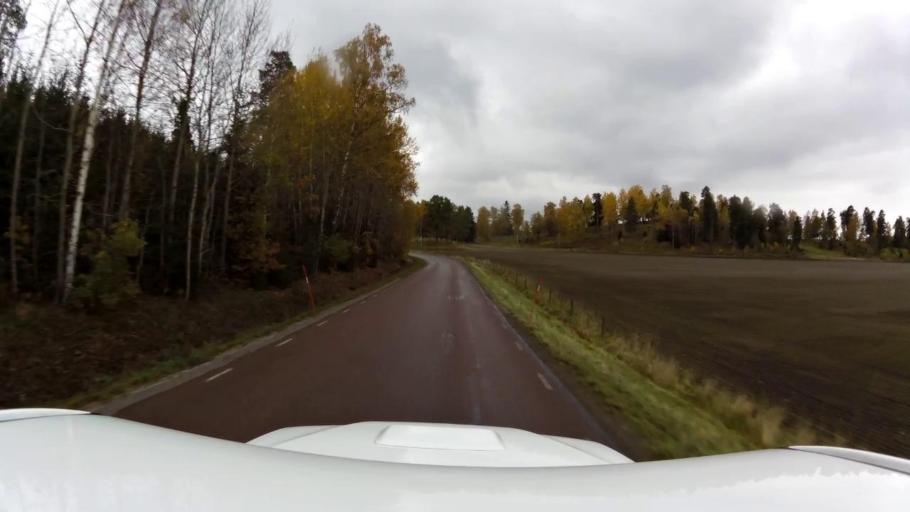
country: SE
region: OEstergoetland
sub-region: Linkopings Kommun
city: Ljungsbro
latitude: 58.5366
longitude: 15.5244
